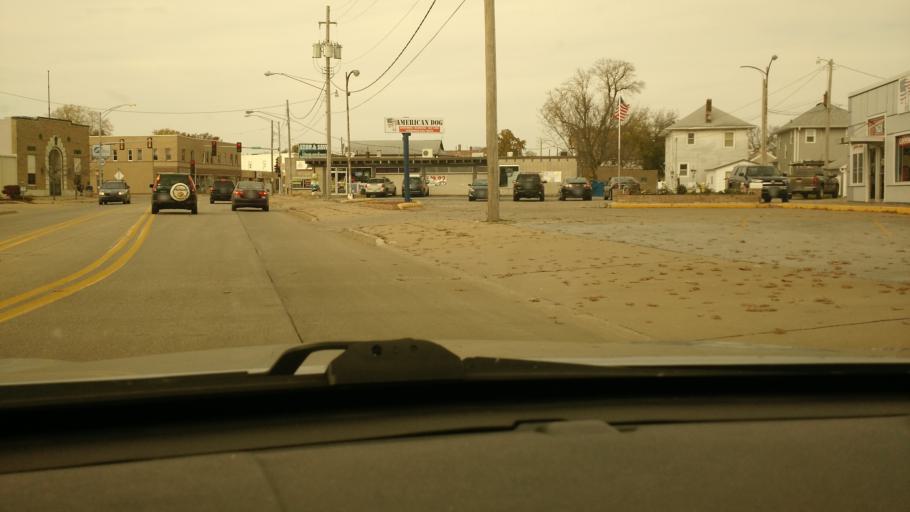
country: US
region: Illinois
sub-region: Rock Island County
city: Moline
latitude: 41.4958
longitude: -90.5151
